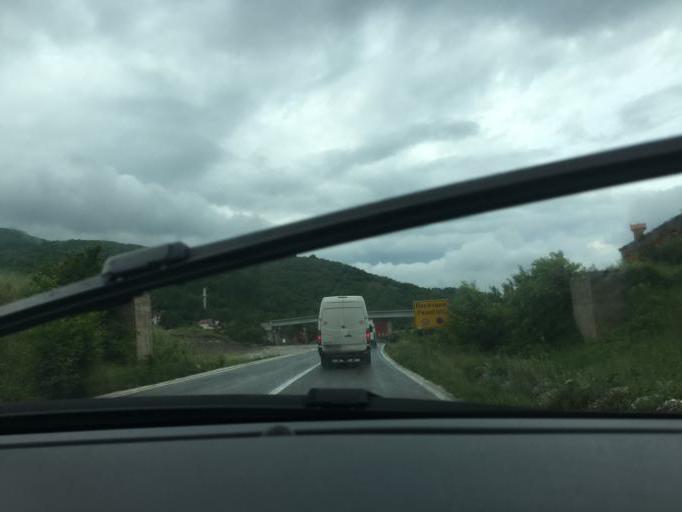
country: MK
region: Debarca
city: Belcista
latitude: 41.3229
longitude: 20.7921
